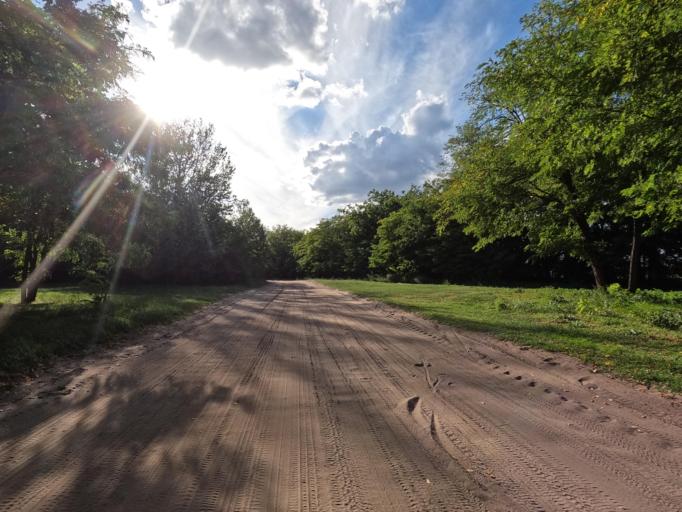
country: HU
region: Tolna
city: Paks
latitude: 46.6183
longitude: 18.8292
